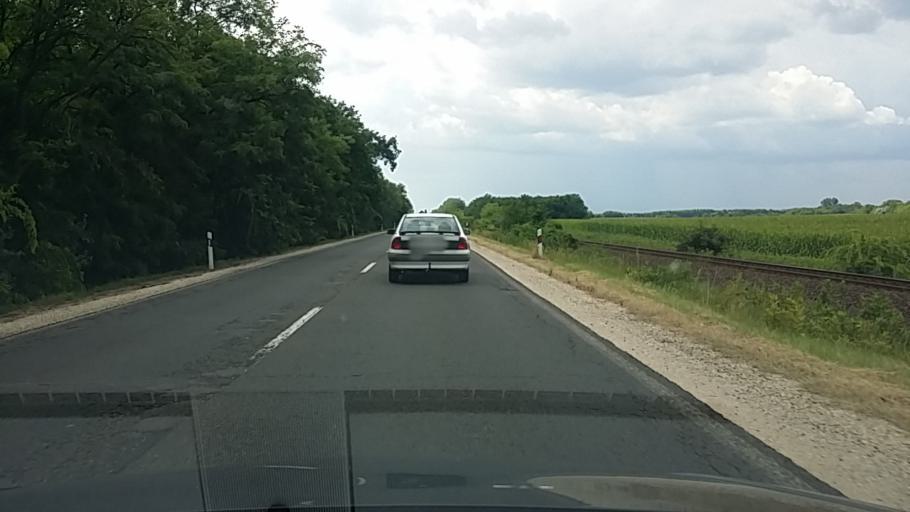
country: HU
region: Pest
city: Ujhartyan
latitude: 47.1677
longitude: 19.3733
